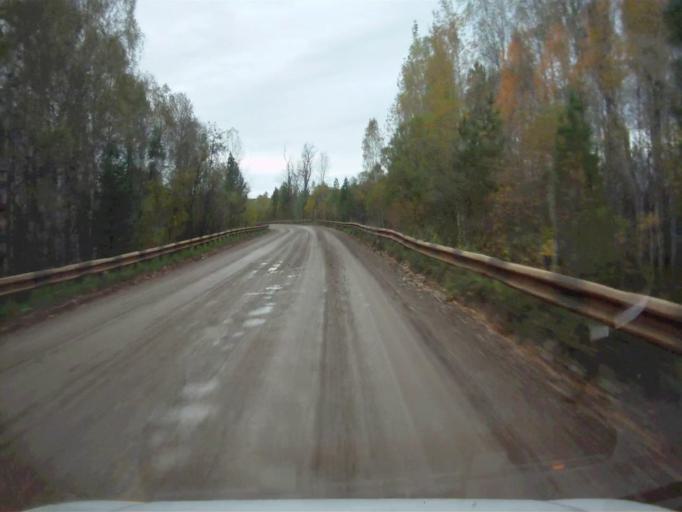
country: RU
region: Chelyabinsk
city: Nyazepetrovsk
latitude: 56.1300
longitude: 59.3270
